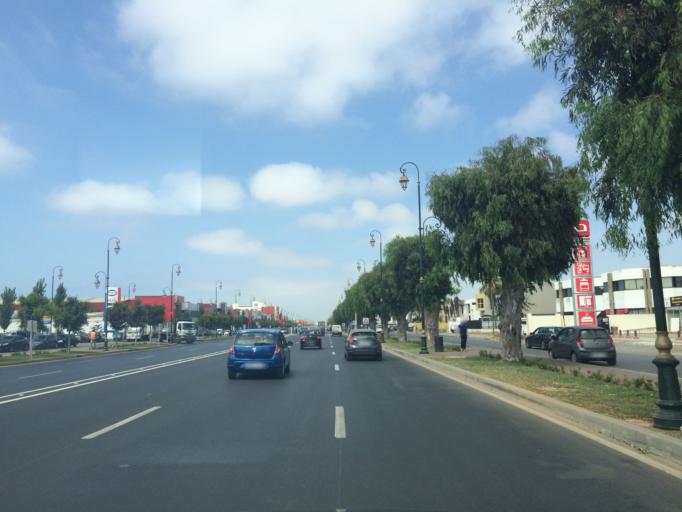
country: MA
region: Rabat-Sale-Zemmour-Zaer
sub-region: Rabat
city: Rabat
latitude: 33.9788
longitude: -6.8750
